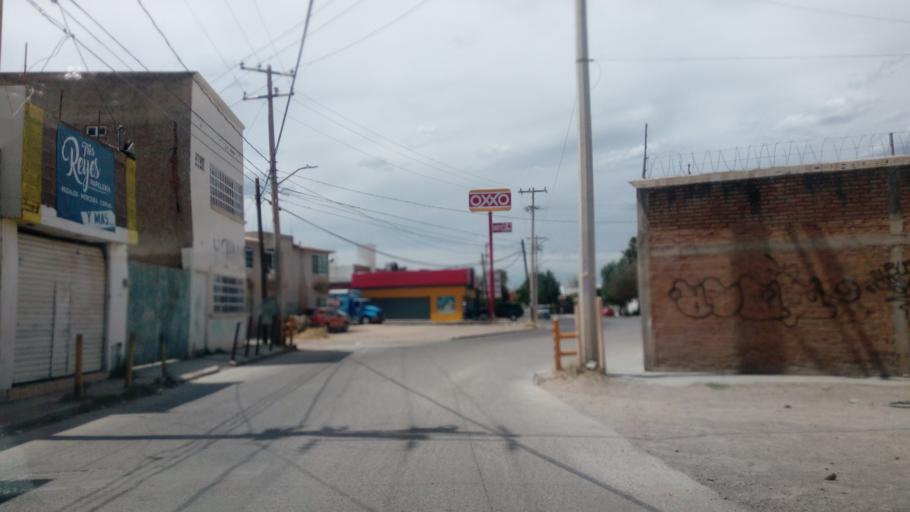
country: MX
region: Durango
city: Victoria de Durango
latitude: 23.9946
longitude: -104.6469
